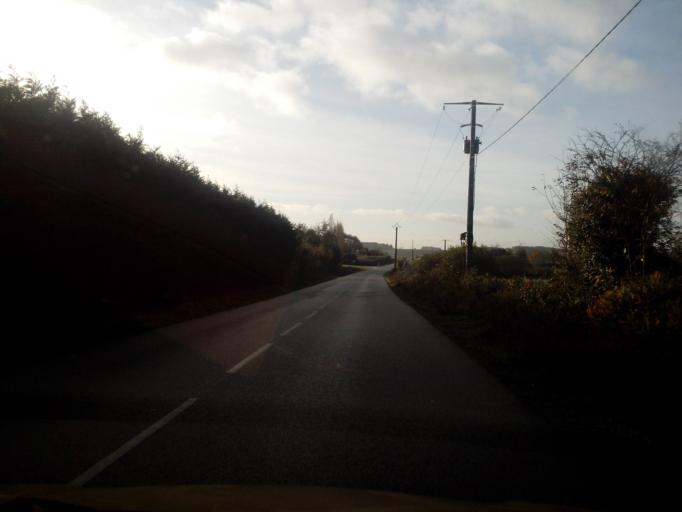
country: FR
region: Brittany
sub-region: Departement du Morbihan
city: Meneac
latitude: 48.1292
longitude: -2.4593
